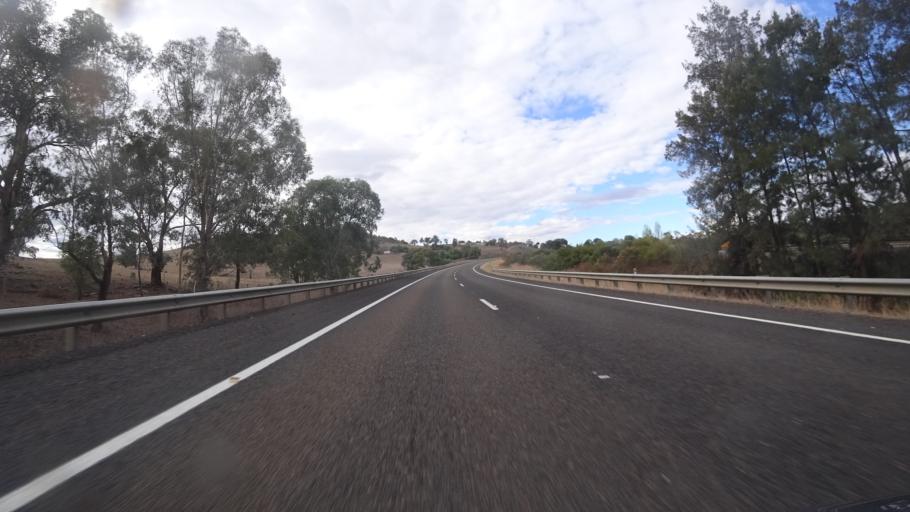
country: AU
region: New South Wales
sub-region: Gundagai
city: Gundagai
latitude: -35.0550
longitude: 148.0954
